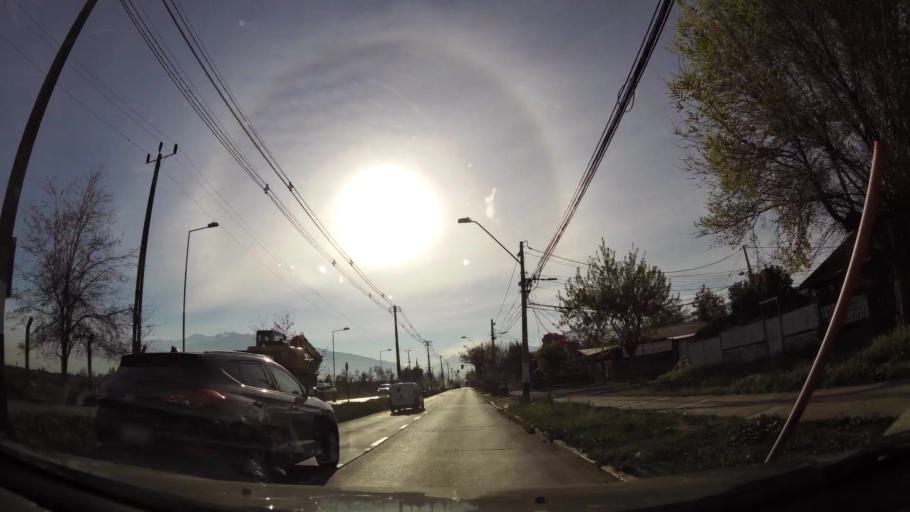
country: CL
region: Santiago Metropolitan
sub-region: Provincia de Cordillera
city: Puente Alto
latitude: -33.6051
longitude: -70.5943
